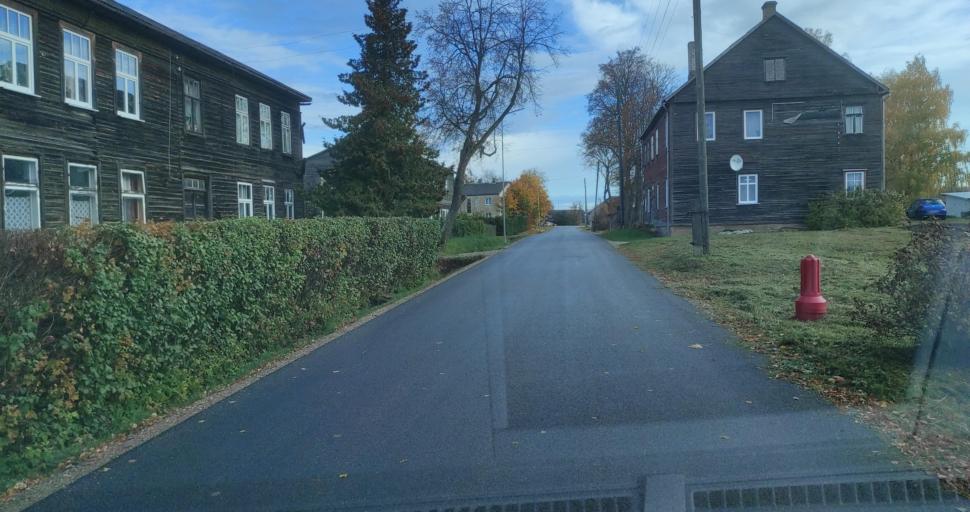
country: LV
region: Skrunda
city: Skrunda
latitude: 56.6712
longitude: 22.0171
